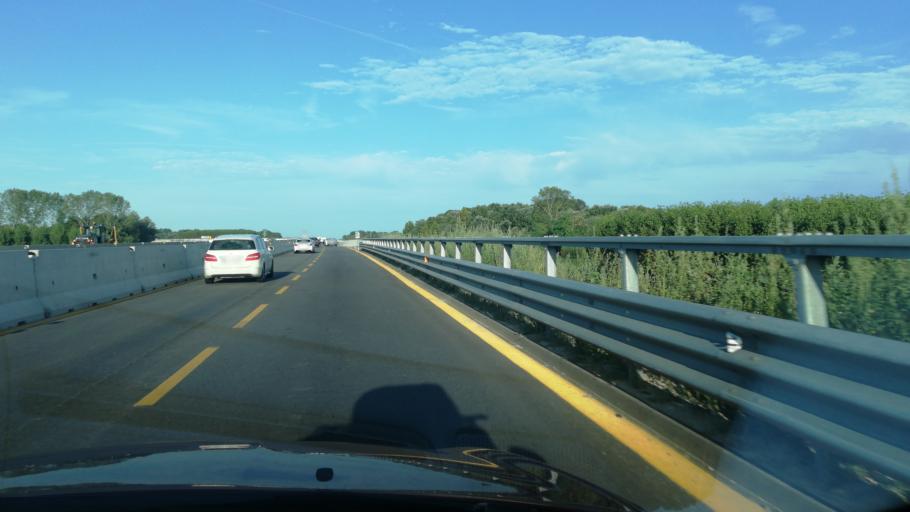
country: IT
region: Friuli Venezia Giulia
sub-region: Provincia di Udine
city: Ronchis
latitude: 45.8154
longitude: 12.9968
